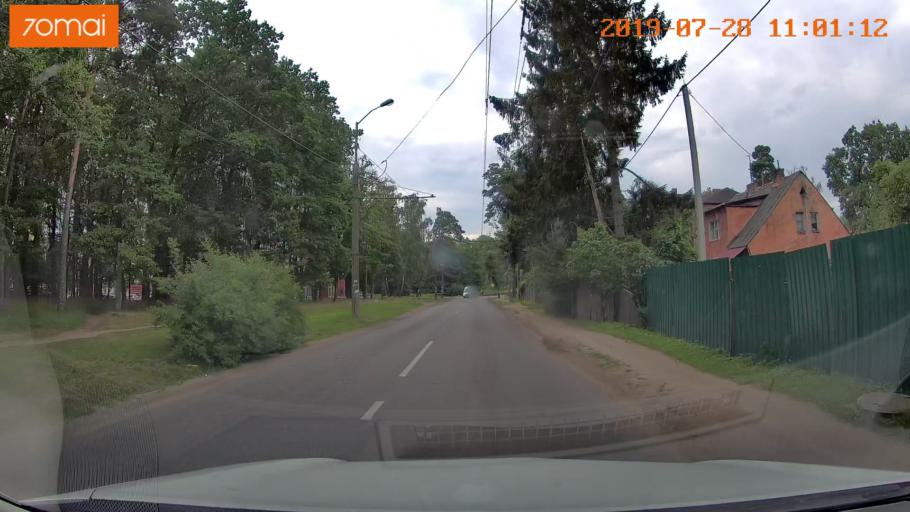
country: RU
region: Kaliningrad
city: Vzmorye
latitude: 54.7230
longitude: 20.3670
